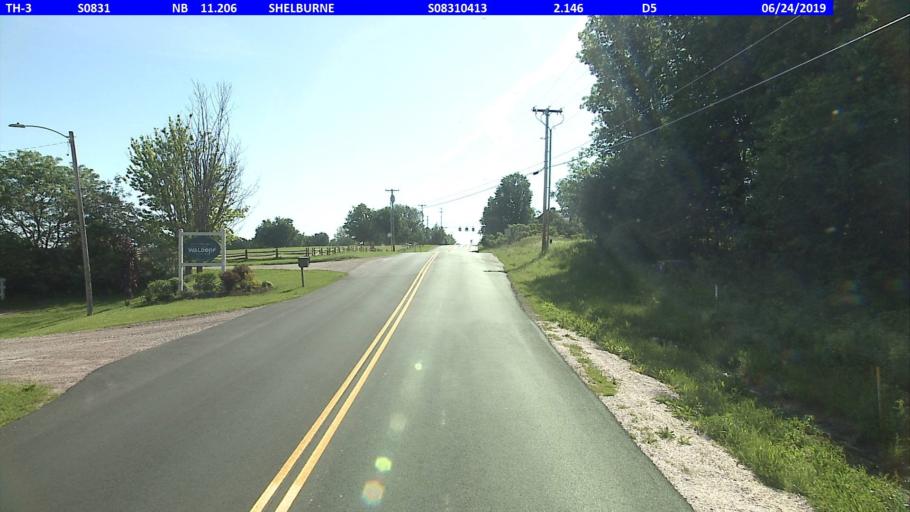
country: US
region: Vermont
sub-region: Chittenden County
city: Burlington
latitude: 44.3690
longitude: -73.2344
